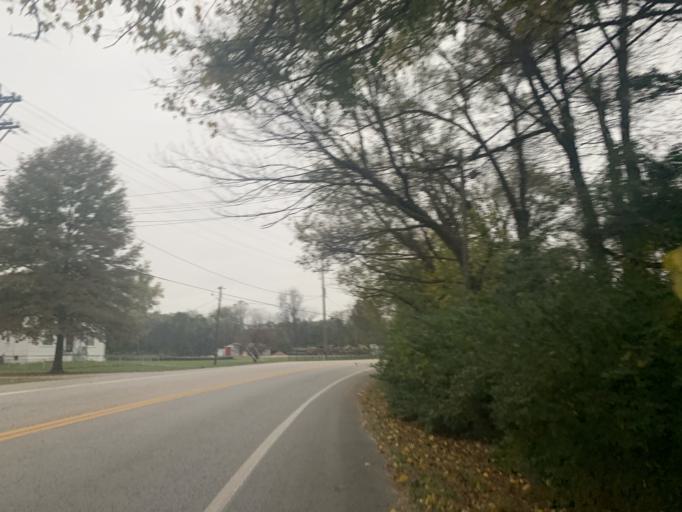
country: US
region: Kentucky
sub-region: Jefferson County
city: Shively
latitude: 38.2135
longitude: -85.8296
